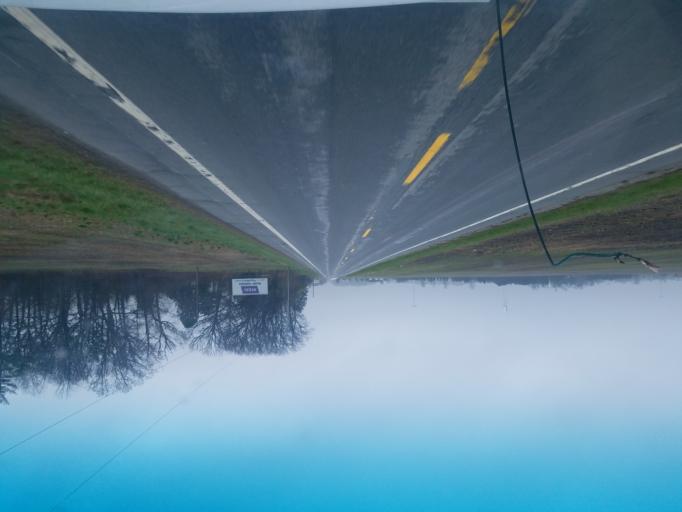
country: US
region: Ohio
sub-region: Wood County
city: Weston
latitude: 41.3722
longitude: -83.7583
